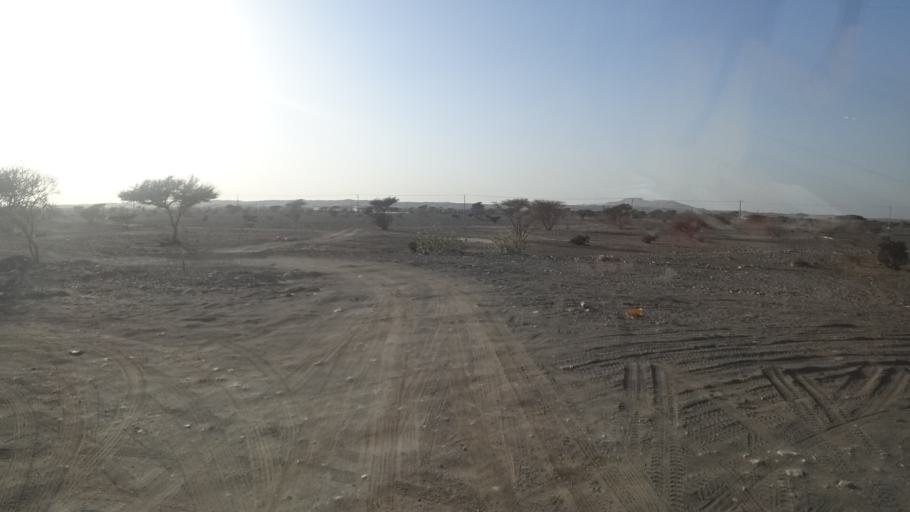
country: OM
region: Ash Sharqiyah
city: Badiyah
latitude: 22.4913
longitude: 58.9268
